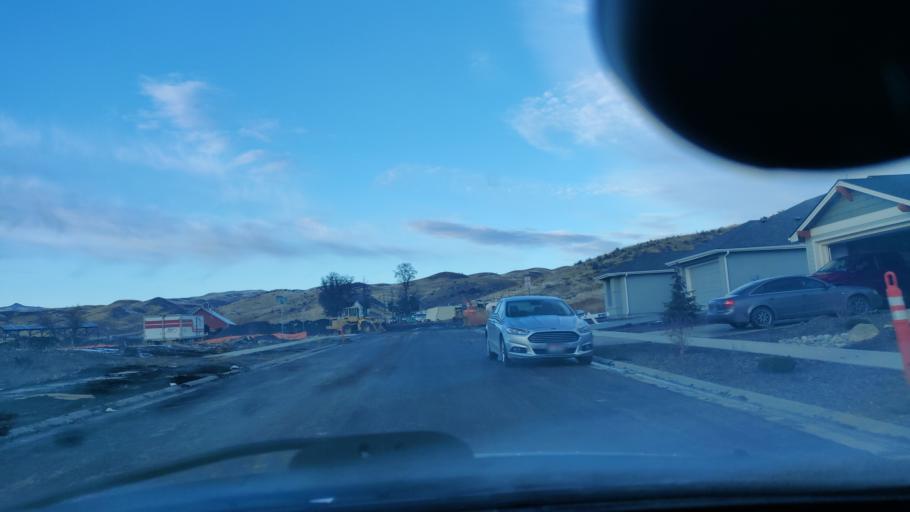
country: US
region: Idaho
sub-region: Ada County
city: Eagle
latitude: 43.7914
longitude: -116.2596
